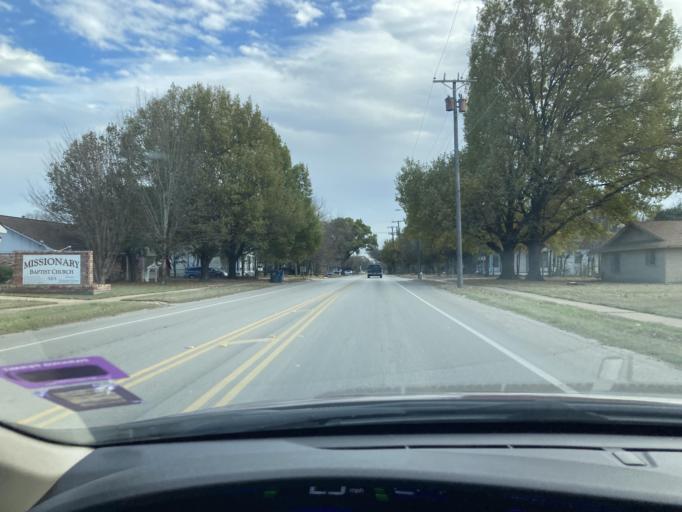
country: US
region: Texas
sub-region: Navarro County
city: Corsicana
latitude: 32.0883
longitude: -96.4673
